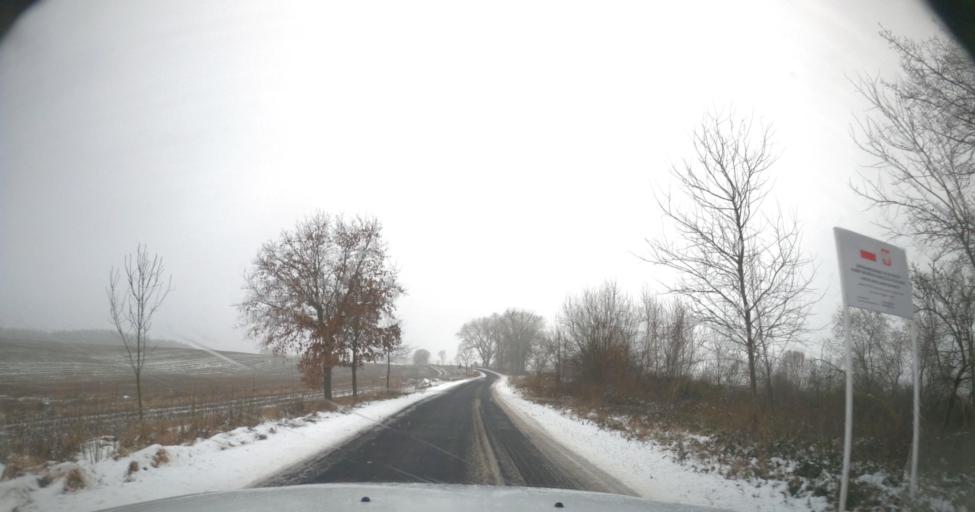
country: PL
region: West Pomeranian Voivodeship
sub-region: Powiat gryficki
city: Gryfice
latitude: 53.8801
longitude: 15.1436
